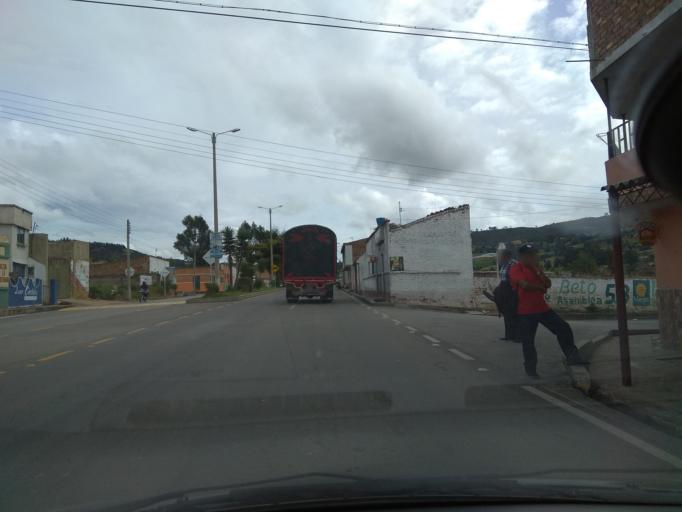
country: CO
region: Boyaca
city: Santa Rosa de Viterbo
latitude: 5.8757
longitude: -72.9858
